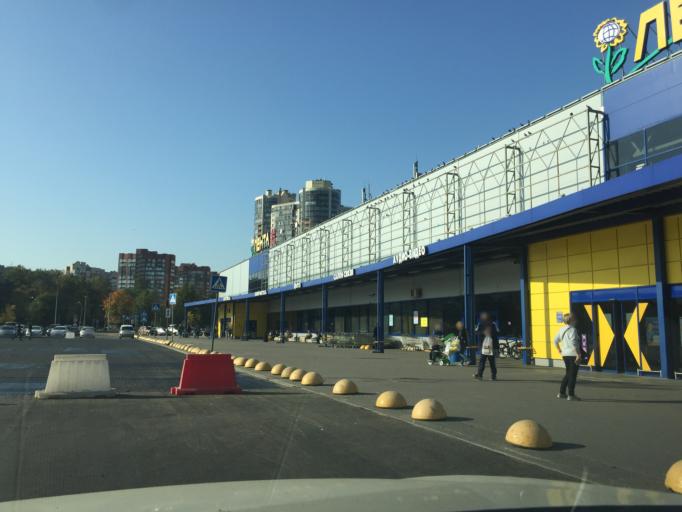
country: RU
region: Leningrad
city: Murino
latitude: 60.0301
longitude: 30.4362
